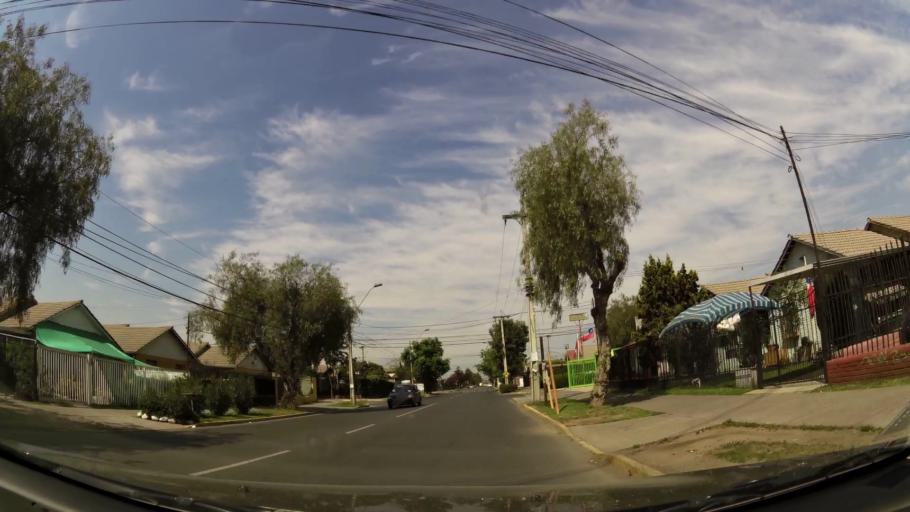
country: CL
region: Santiago Metropolitan
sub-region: Provincia de Cordillera
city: Puente Alto
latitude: -33.5877
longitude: -70.5862
